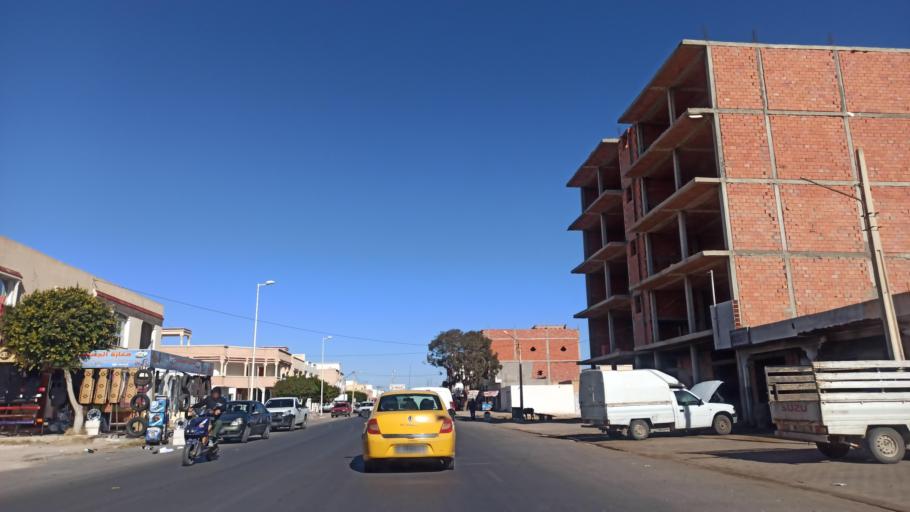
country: TN
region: Sidi Bu Zayd
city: Bi'r al Hufayy
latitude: 34.9208
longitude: 9.1878
